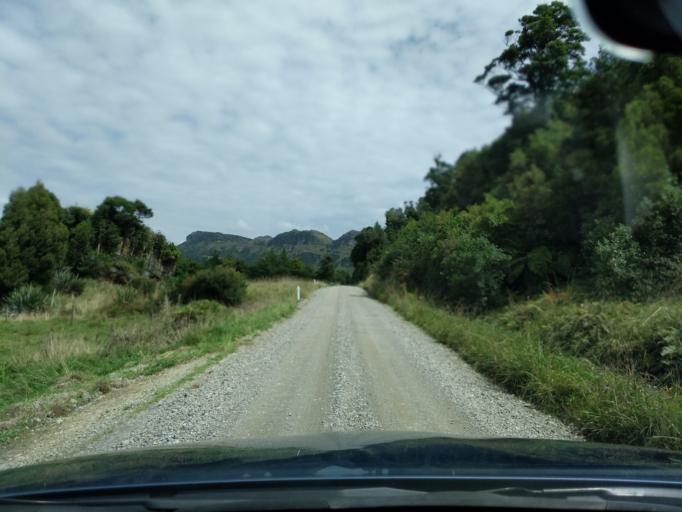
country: NZ
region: Tasman
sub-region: Tasman District
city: Takaka
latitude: -40.6507
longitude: 172.4667
